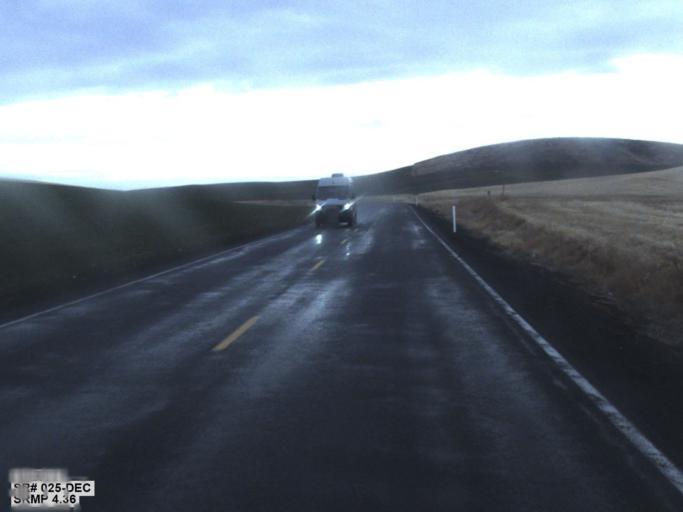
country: US
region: Washington
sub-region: Lincoln County
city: Davenport
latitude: 47.7155
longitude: -118.1515
